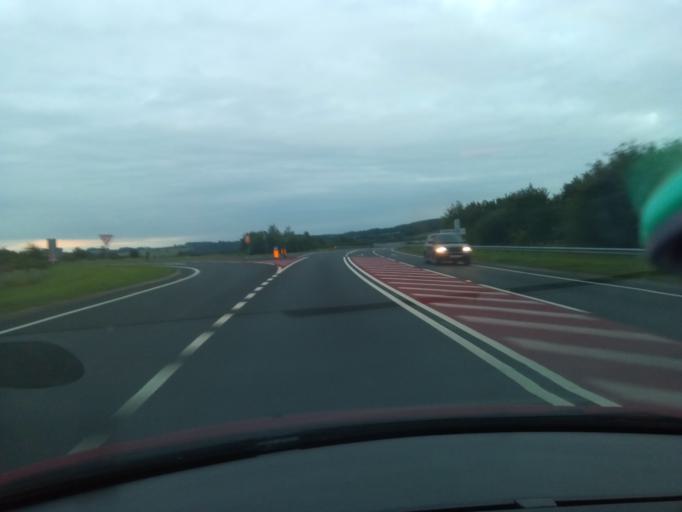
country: GB
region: England
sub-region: Northumberland
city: Bardon Mill
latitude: 54.9692
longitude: -2.2586
